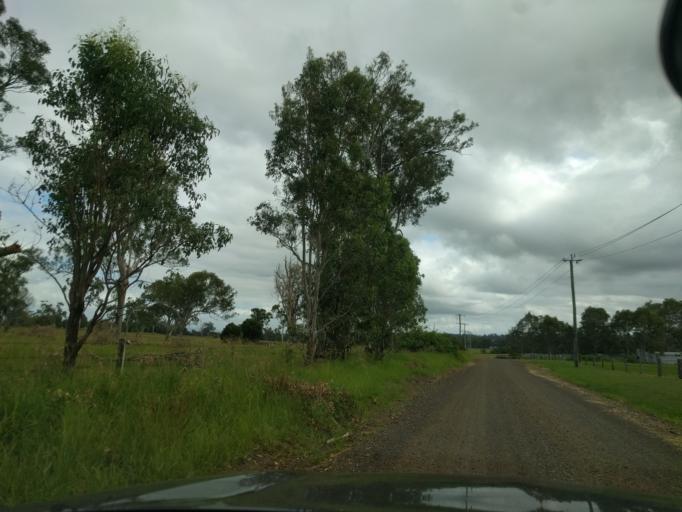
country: AU
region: Queensland
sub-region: Logan
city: Cedar Vale
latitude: -28.0073
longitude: 152.9958
